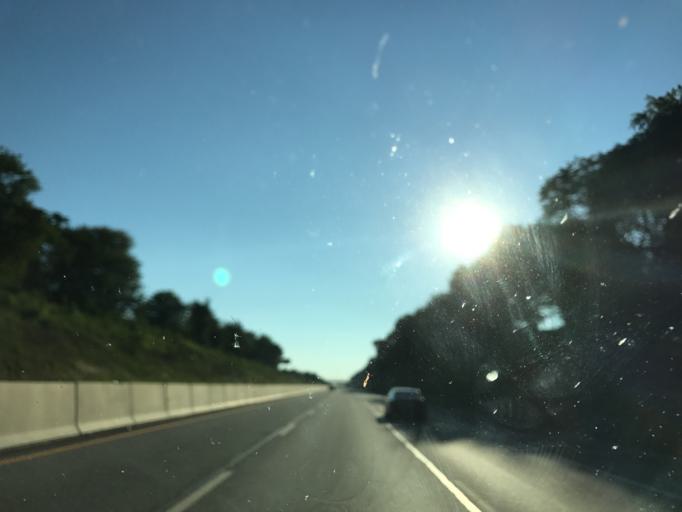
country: US
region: Pennsylvania
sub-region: Bucks County
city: Warminster Heights
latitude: 40.1624
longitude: -75.0813
